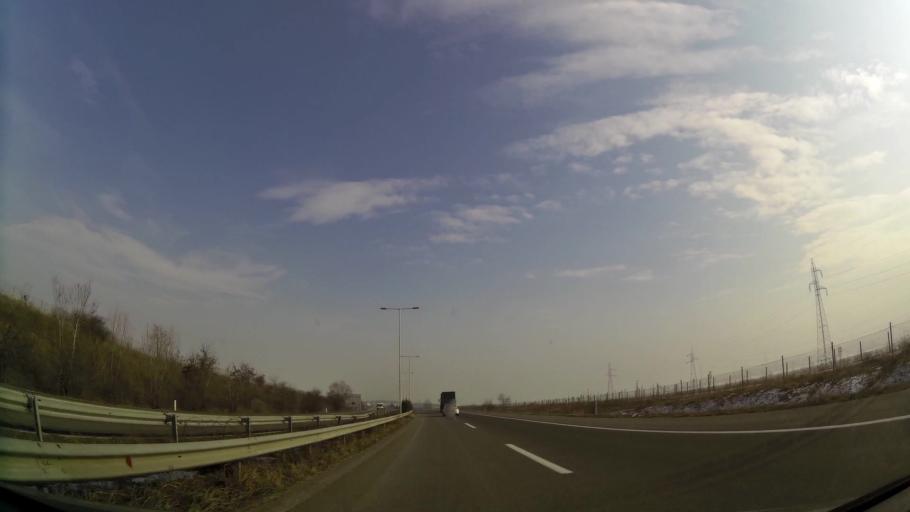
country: MK
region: Butel
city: Butel
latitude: 42.0325
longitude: 21.4789
